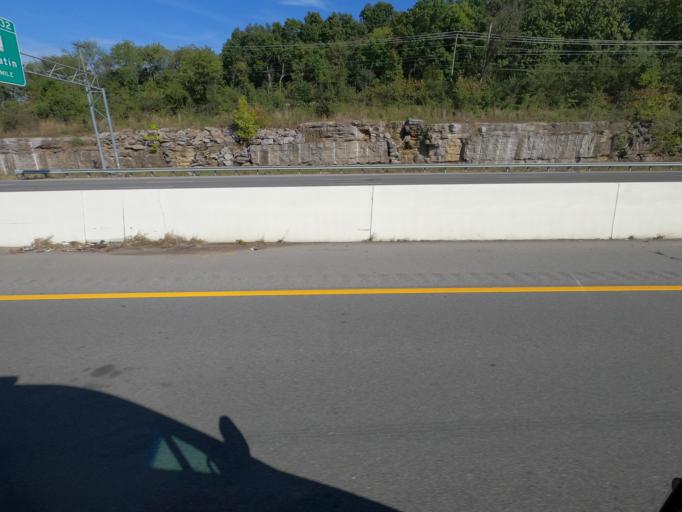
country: US
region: Tennessee
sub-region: Wilson County
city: Lebanon
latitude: 36.1838
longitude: -86.3933
